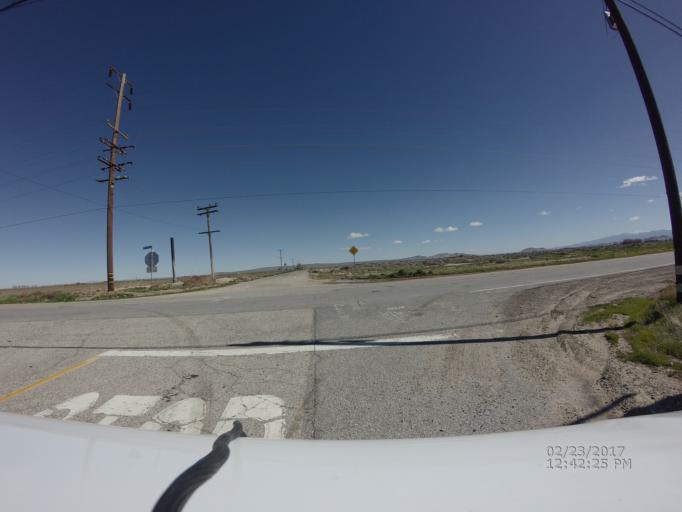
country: US
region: California
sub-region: Kern County
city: Edwards Air Force Base
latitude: 34.7489
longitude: -117.9700
